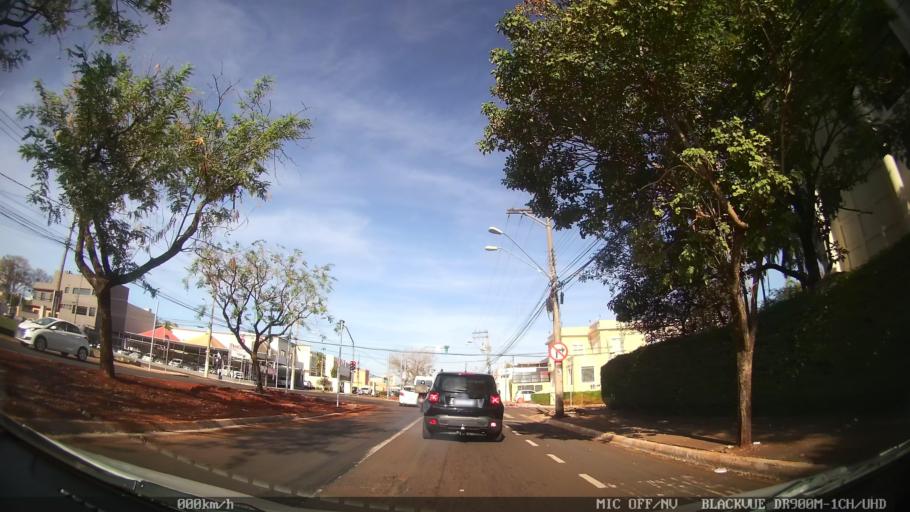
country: BR
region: Sao Paulo
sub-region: Ribeirao Preto
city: Ribeirao Preto
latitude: -21.2055
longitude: -47.8216
